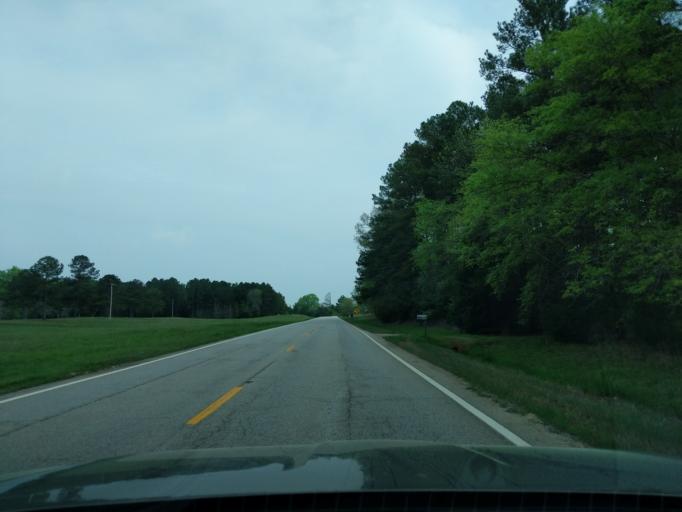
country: US
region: Georgia
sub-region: Lincoln County
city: Lincolnton
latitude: 33.7997
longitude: -82.3881
